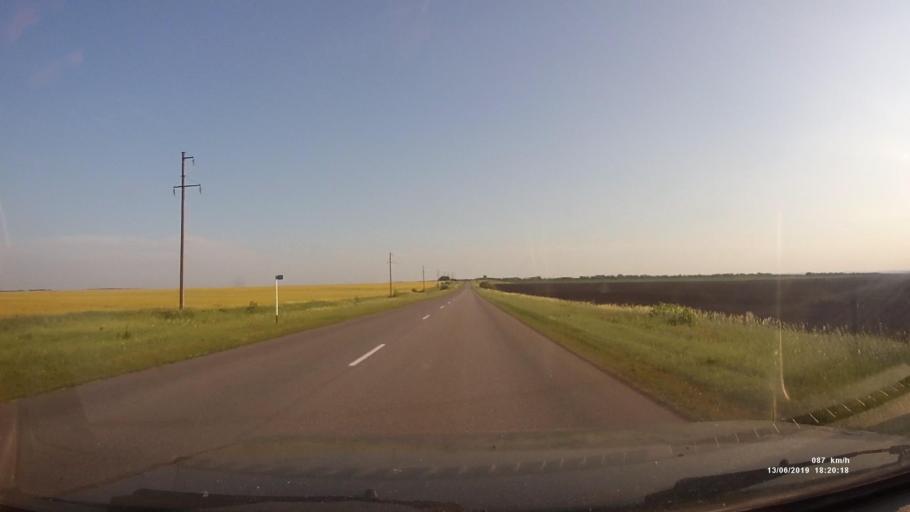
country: RU
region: Rostov
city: Kazanskaya
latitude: 49.8856
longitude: 41.3002
